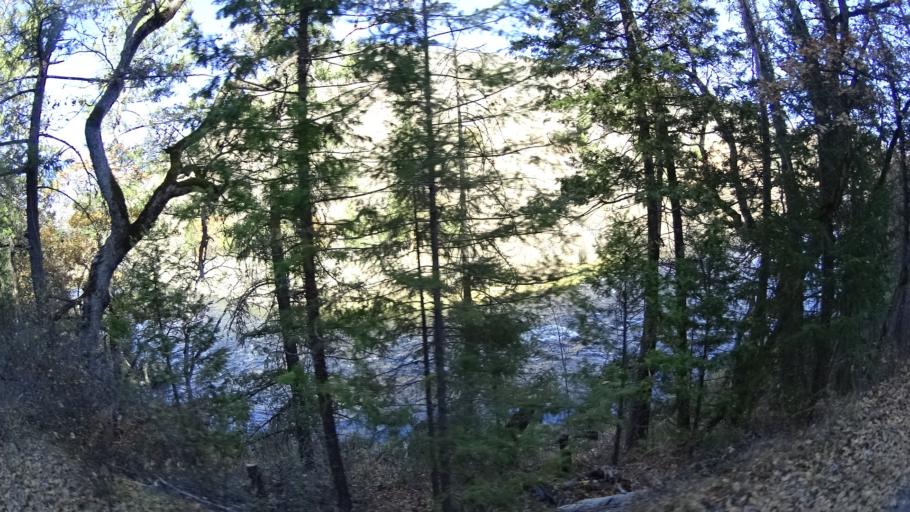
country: US
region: California
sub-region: Siskiyou County
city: Yreka
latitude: 41.8536
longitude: -122.7680
